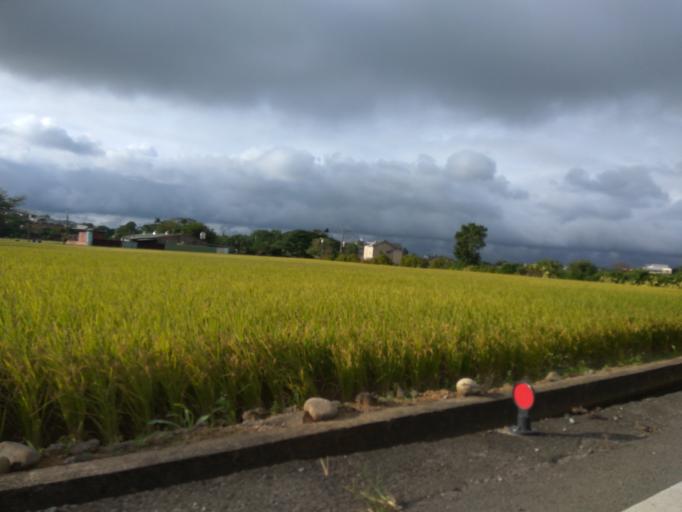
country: TW
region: Taiwan
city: Daxi
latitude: 24.9417
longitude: 121.2001
